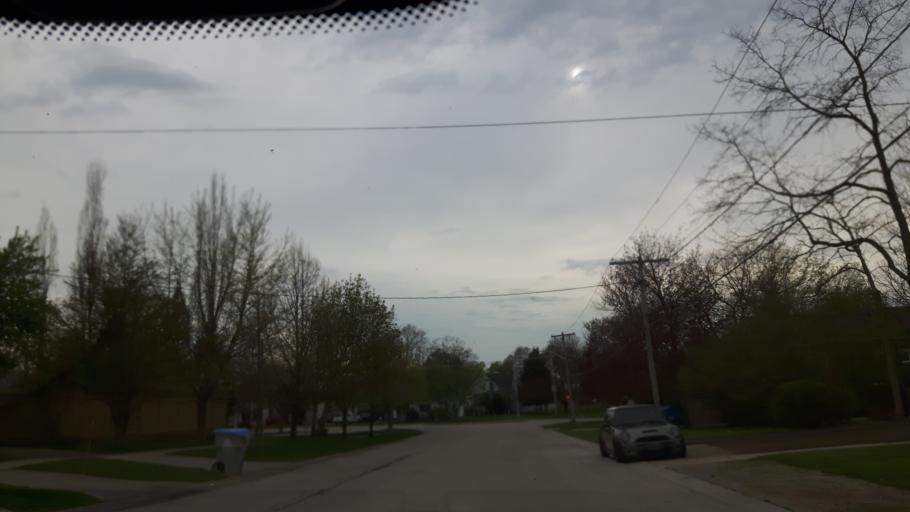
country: CA
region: Ontario
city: Goderich
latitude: 43.7456
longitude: -81.7133
